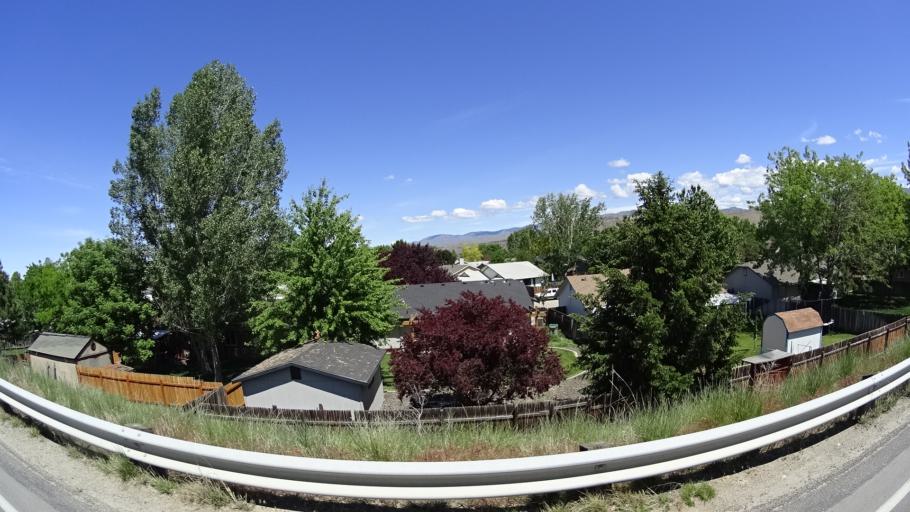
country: US
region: Idaho
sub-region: Ada County
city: Boise
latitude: 43.5607
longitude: -116.1649
